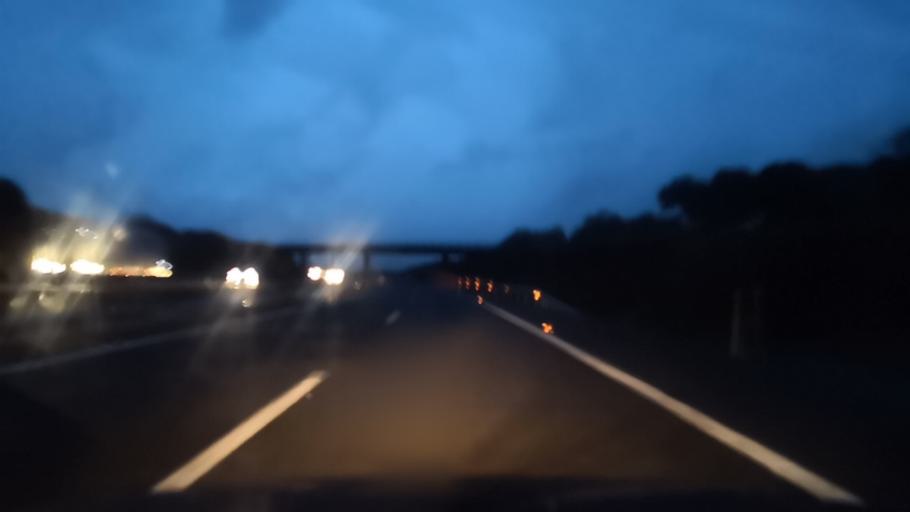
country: ES
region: Extremadura
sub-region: Provincia de Caceres
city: Aldea del Cano
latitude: 39.3588
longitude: -6.3390
